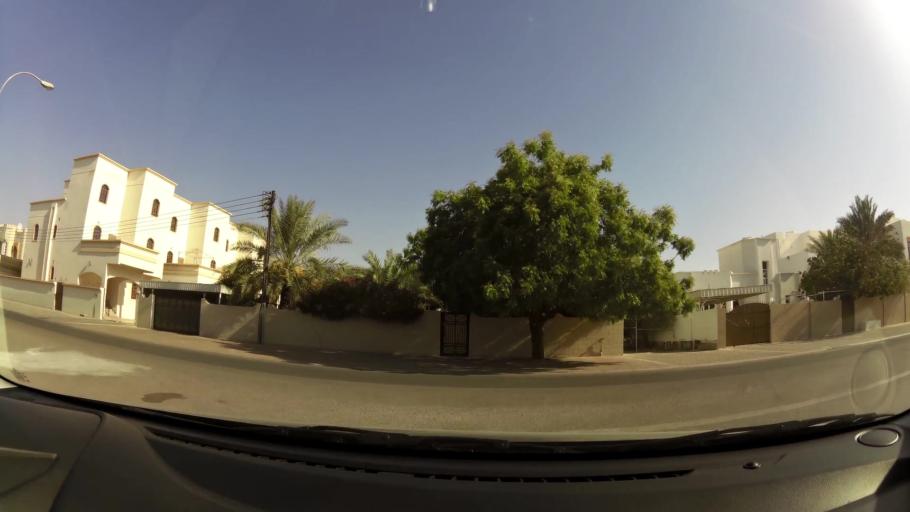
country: OM
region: Muhafazat Masqat
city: As Sib al Jadidah
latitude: 23.6159
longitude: 58.2113
